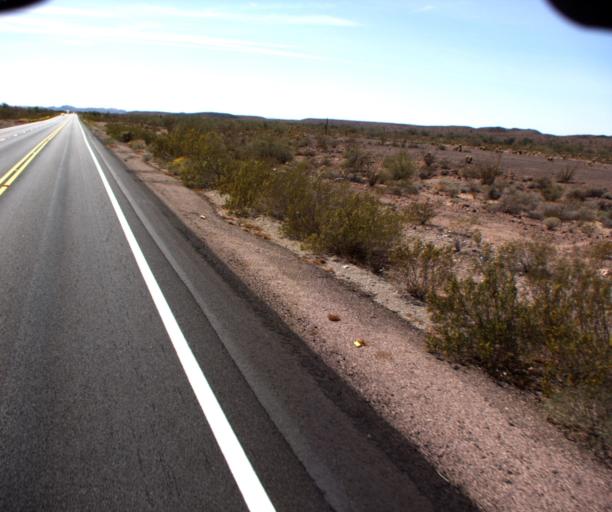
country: US
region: Arizona
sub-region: La Paz County
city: Quartzsite
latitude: 33.2260
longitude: -114.2562
